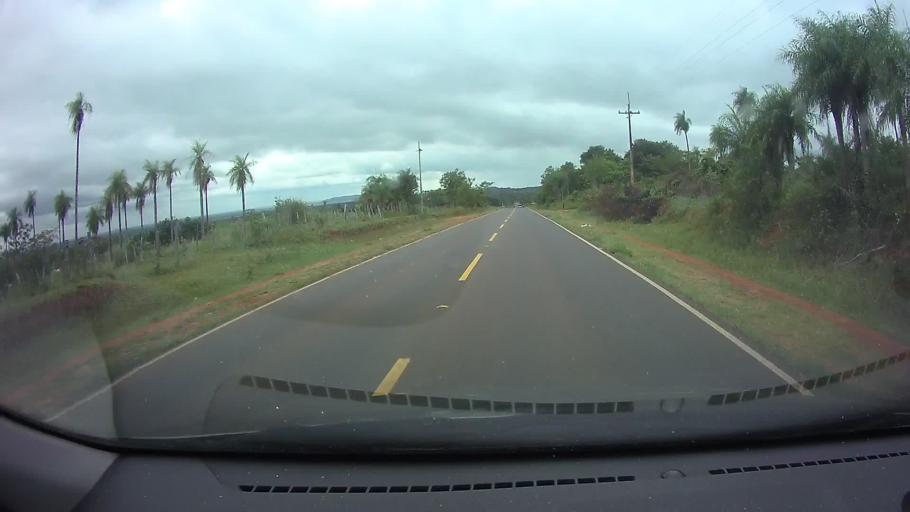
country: PY
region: Paraguari
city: Carapegua
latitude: -25.7283
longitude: -57.3133
